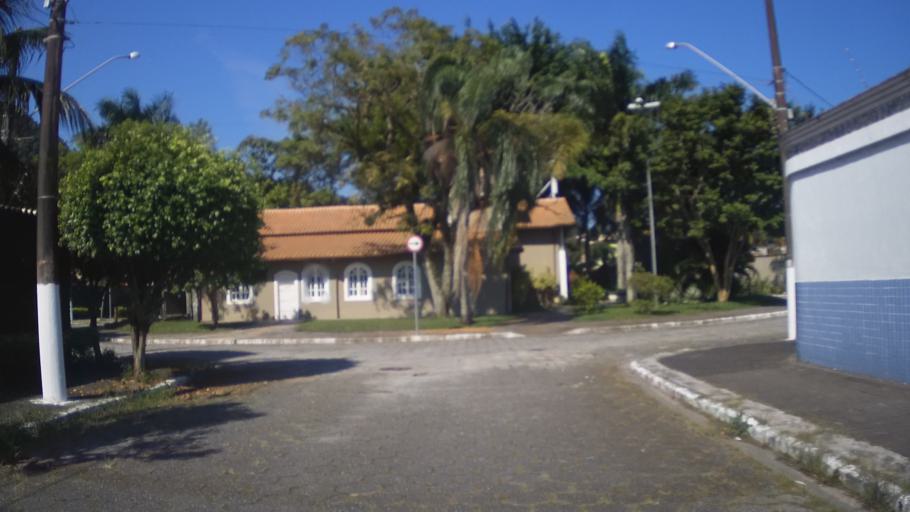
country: BR
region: Sao Paulo
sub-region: Praia Grande
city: Praia Grande
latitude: -24.0064
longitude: -46.4034
